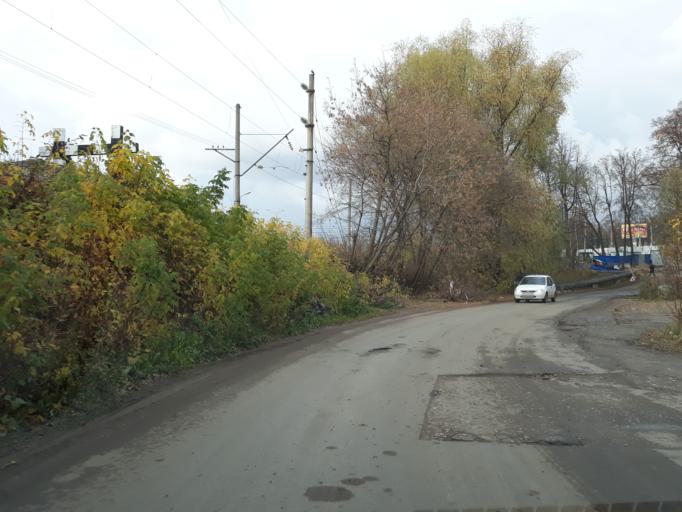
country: RU
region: Nizjnij Novgorod
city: Nizhniy Novgorod
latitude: 56.2546
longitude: 43.9722
